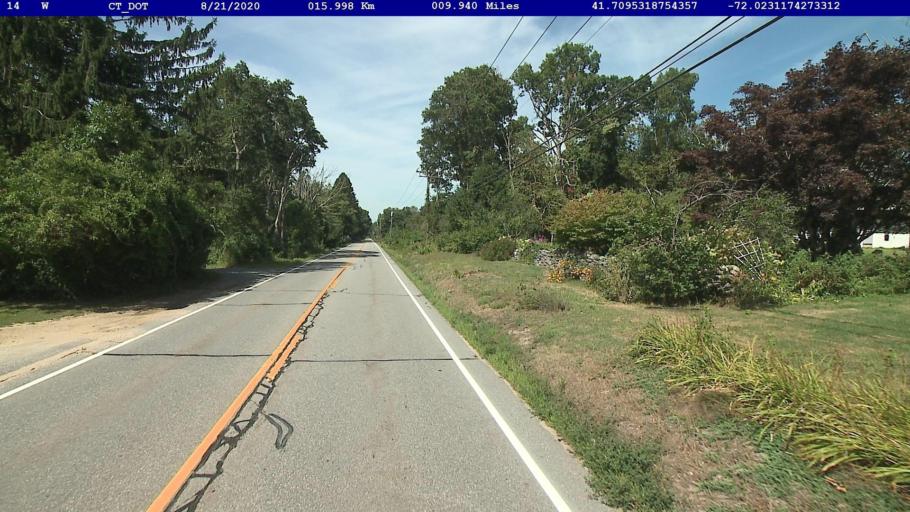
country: US
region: Connecticut
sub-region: Windham County
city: Plainfield Village
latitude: 41.7096
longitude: -72.0231
